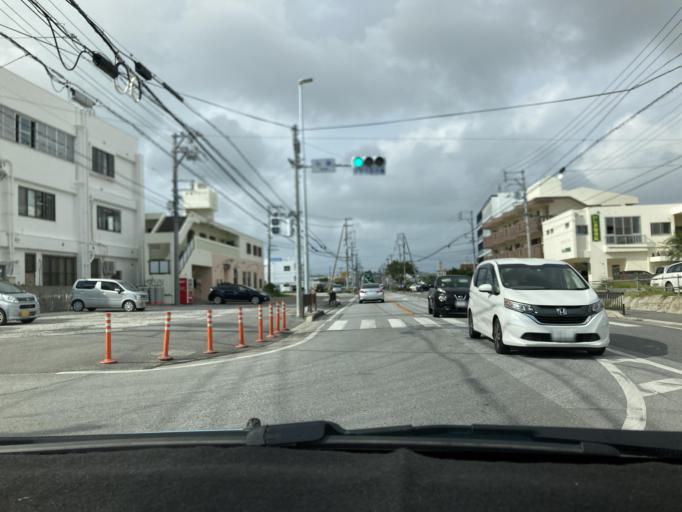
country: JP
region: Okinawa
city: Tomigusuku
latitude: 26.1647
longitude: 127.6686
